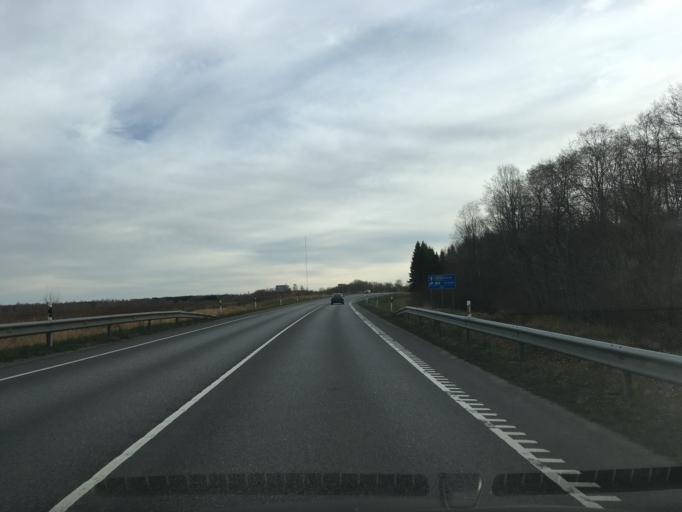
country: EE
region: Ida-Virumaa
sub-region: Narva-Joesuu linn
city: Narva-Joesuu
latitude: 59.3784
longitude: 27.9274
